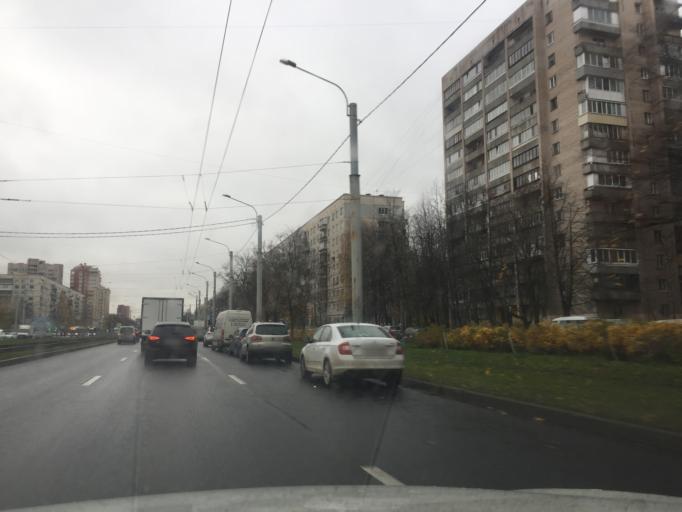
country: RU
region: St.-Petersburg
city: Grazhdanka
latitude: 60.0419
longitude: 30.4004
